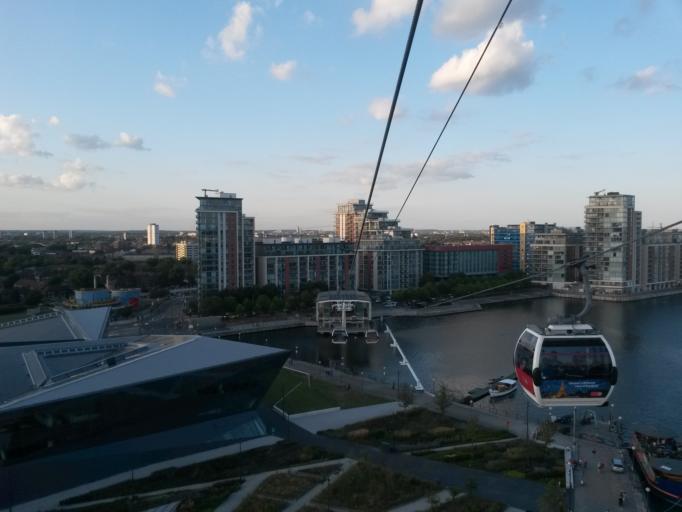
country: GB
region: England
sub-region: Greater London
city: Poplar
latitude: 51.5061
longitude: 0.0161
